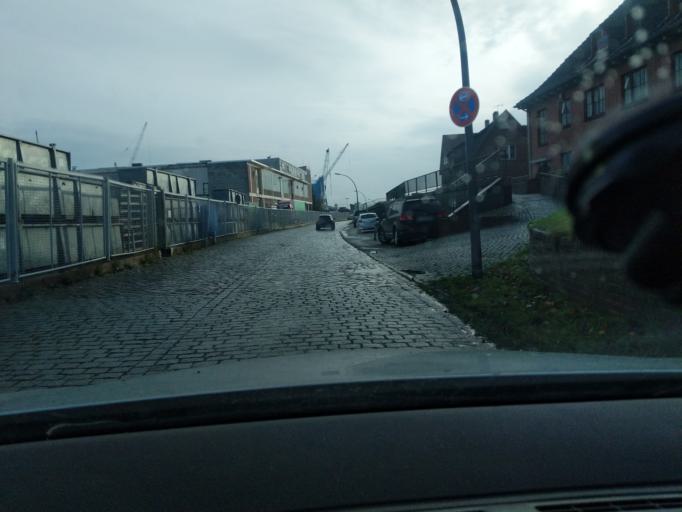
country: DE
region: Lower Saxony
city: Neu Wulmstorf
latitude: 53.5320
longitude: 9.7836
